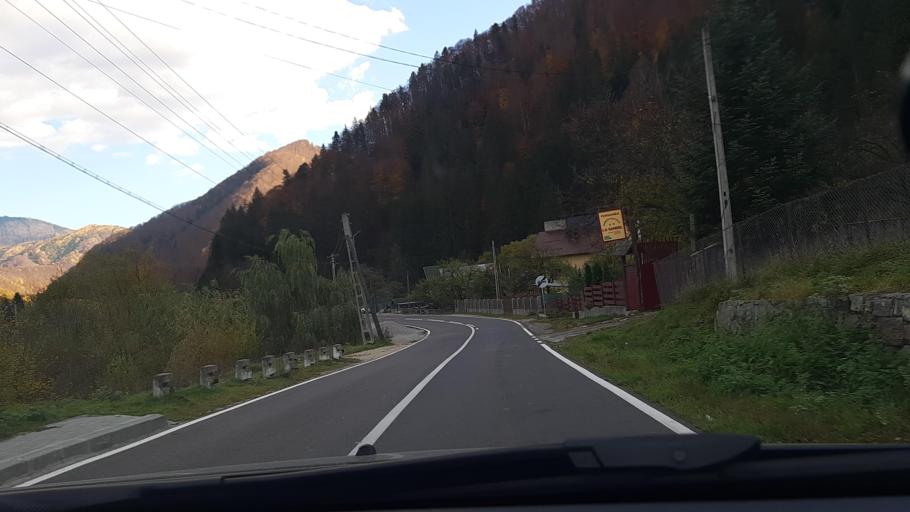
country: RO
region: Valcea
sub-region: Comuna Voineasa
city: Voineasa
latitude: 45.4116
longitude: 23.9649
